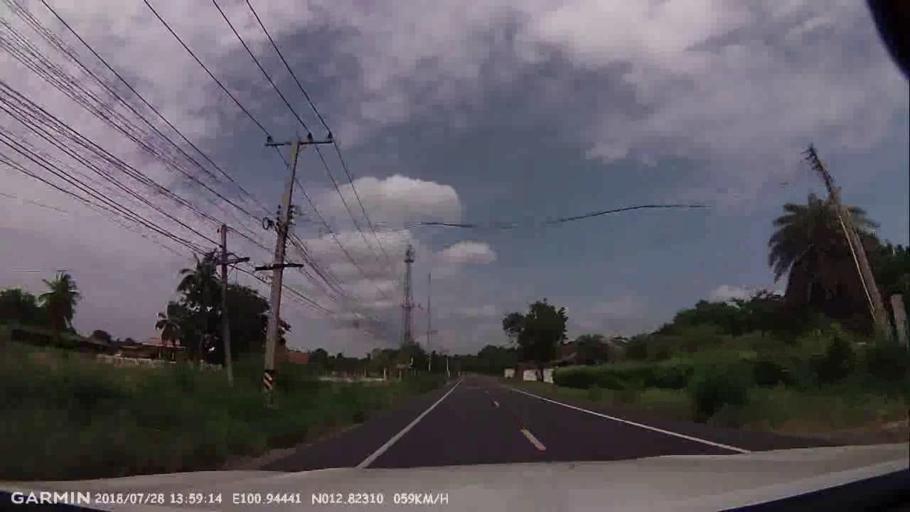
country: TH
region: Chon Buri
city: Phatthaya
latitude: 12.8231
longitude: 100.9445
